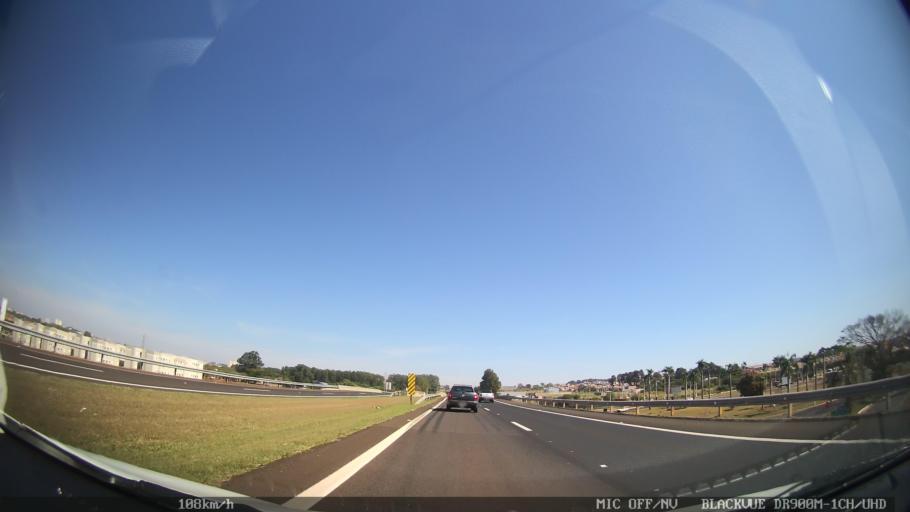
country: BR
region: Sao Paulo
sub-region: Ribeirao Preto
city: Ribeirao Preto
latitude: -21.1167
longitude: -47.8274
